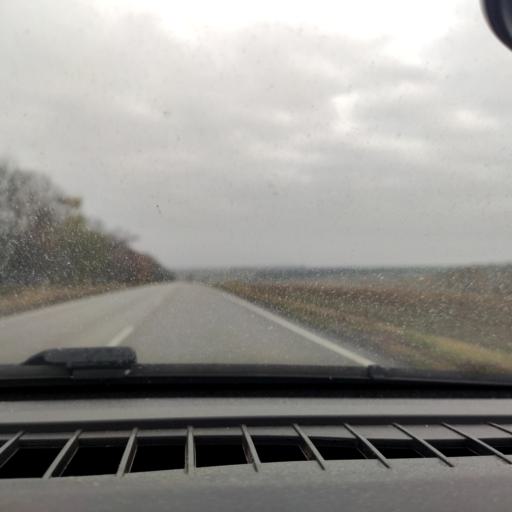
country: RU
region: Belgorod
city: Ilovka
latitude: 50.7632
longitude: 38.7430
